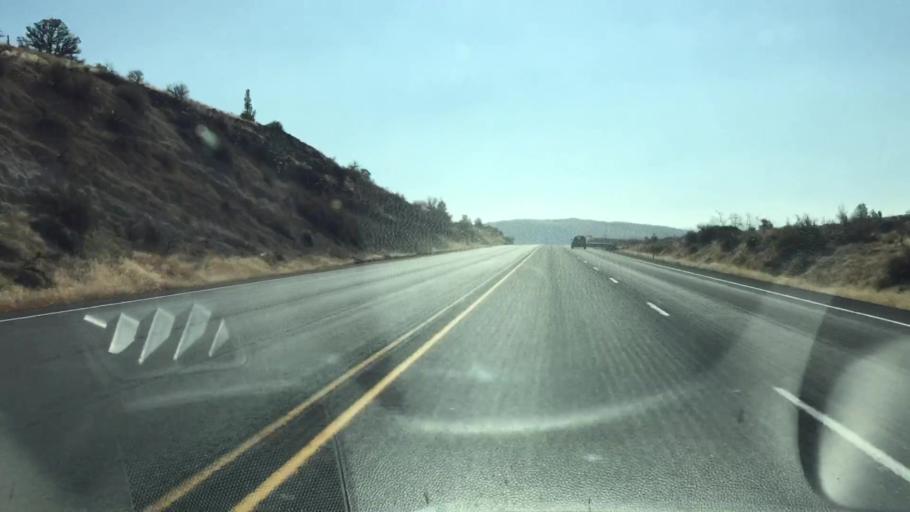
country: US
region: Oregon
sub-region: Jefferson County
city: Madras
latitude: 44.7633
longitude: -120.9951
